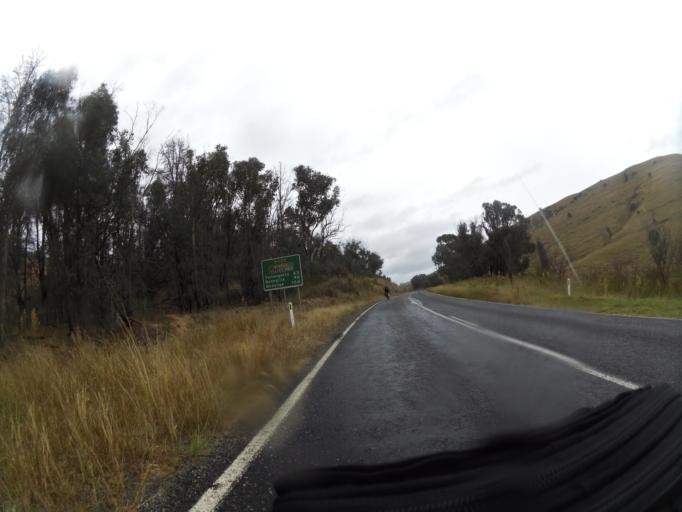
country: AU
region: New South Wales
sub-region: Greater Hume Shire
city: Holbrook
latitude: -36.2240
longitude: 147.7270
